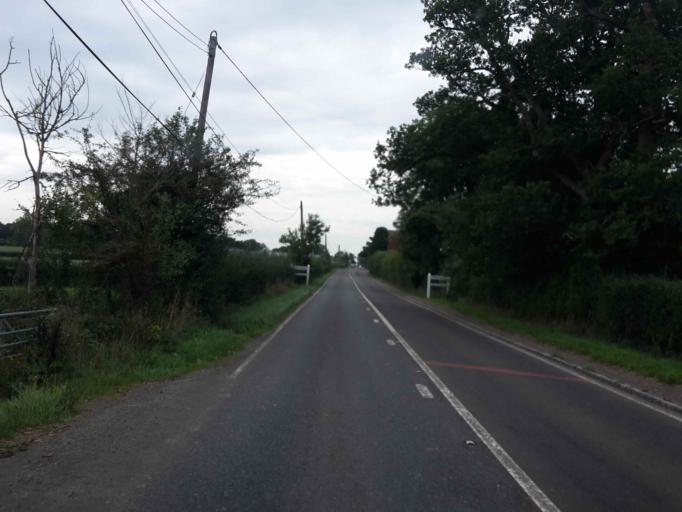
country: GB
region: England
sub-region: West Sussex
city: Billingshurst
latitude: 51.0491
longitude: -0.4319
